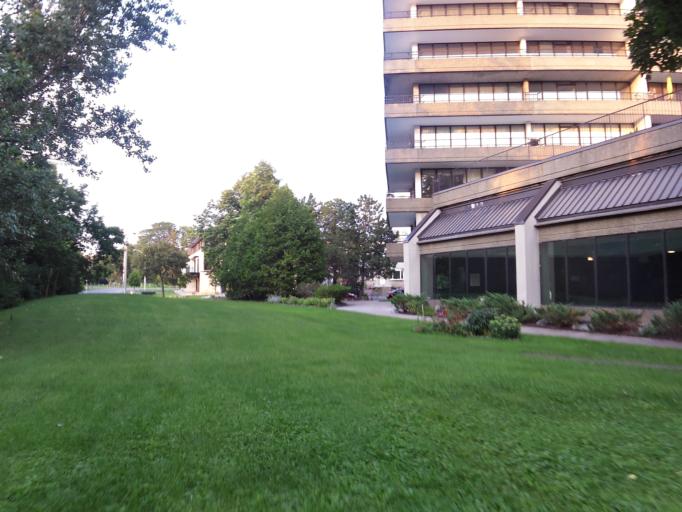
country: CA
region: Ontario
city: Ottawa
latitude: 45.3915
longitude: -75.7603
